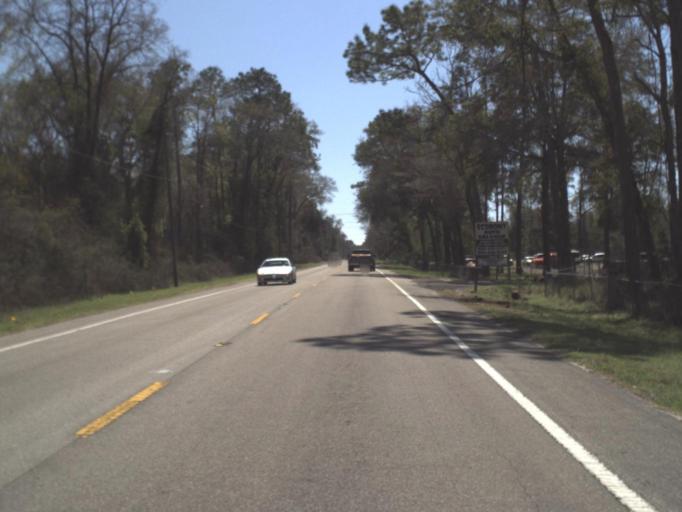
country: US
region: Florida
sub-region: Leon County
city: Woodville
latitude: 30.2508
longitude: -84.2340
